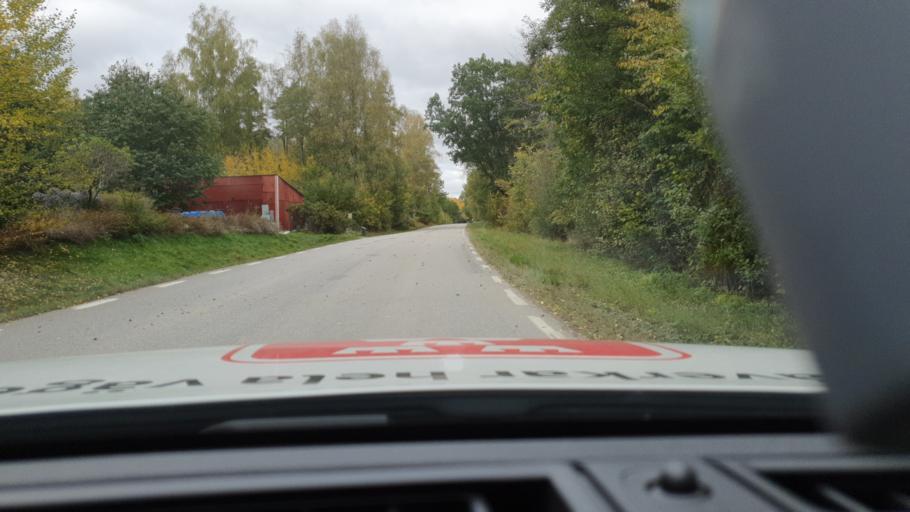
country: SE
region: Stockholm
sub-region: Upplands-Bro Kommun
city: Bro
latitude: 59.4966
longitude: 17.5695
